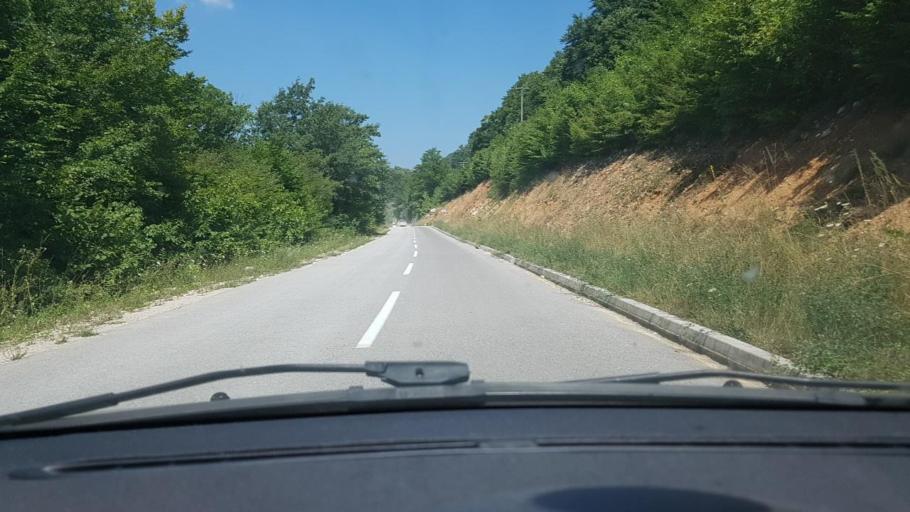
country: BA
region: Federation of Bosnia and Herzegovina
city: Orasac
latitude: 44.5044
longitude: 16.1299
